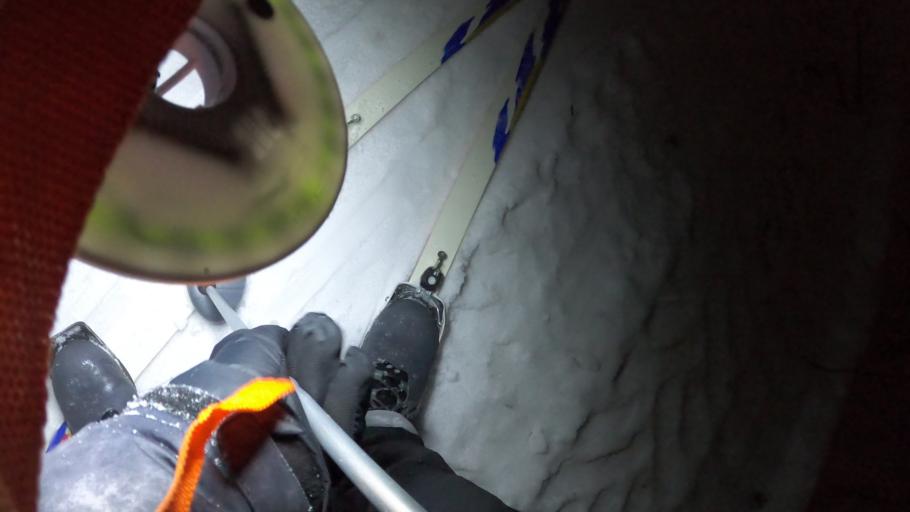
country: RU
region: Moskovskaya
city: Opalikha
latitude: 55.8714
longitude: 37.2281
